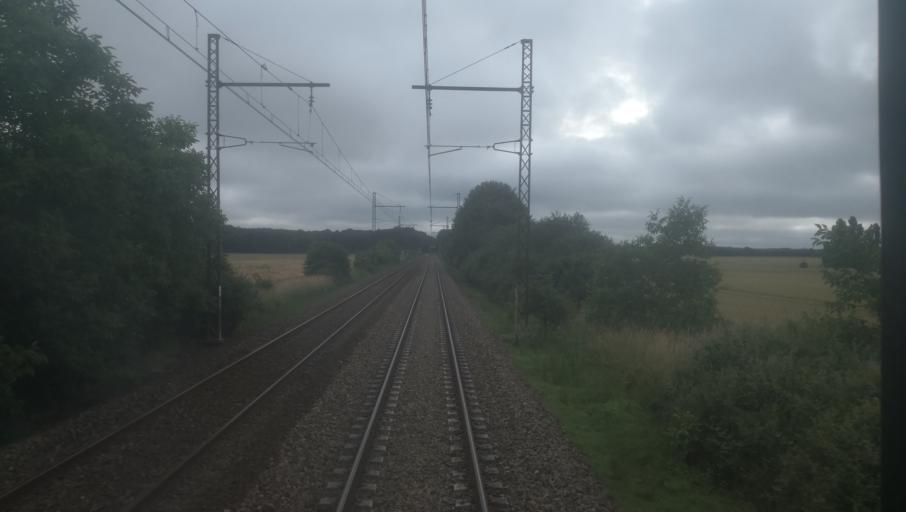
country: FR
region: Centre
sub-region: Departement de l'Indre
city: Montierchaume
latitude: 46.8379
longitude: 1.7652
